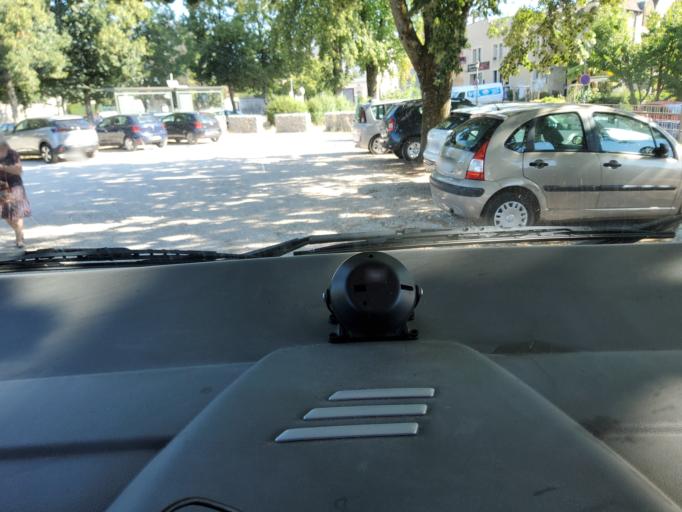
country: FR
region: Franche-Comte
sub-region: Departement du Jura
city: Dole
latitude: 47.0909
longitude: 5.4886
